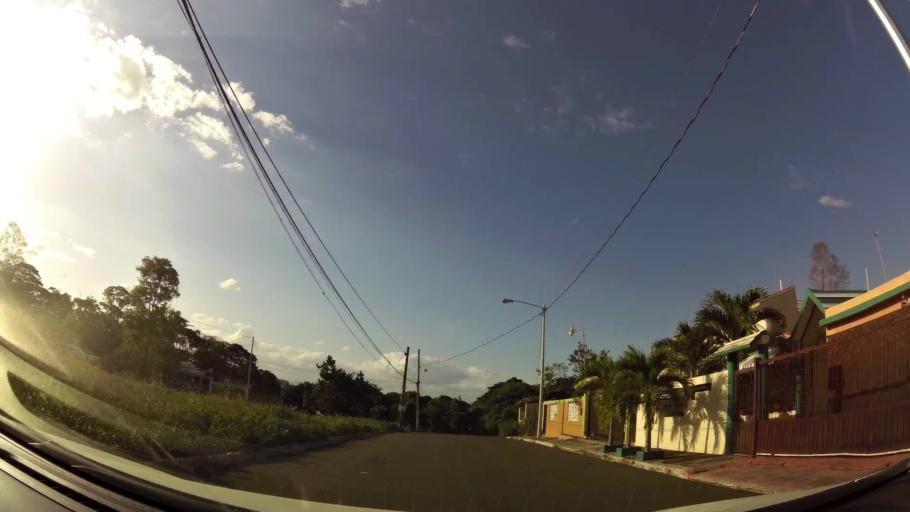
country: DO
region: Nacional
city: Ensanche Luperon
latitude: 18.5481
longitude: -69.9162
